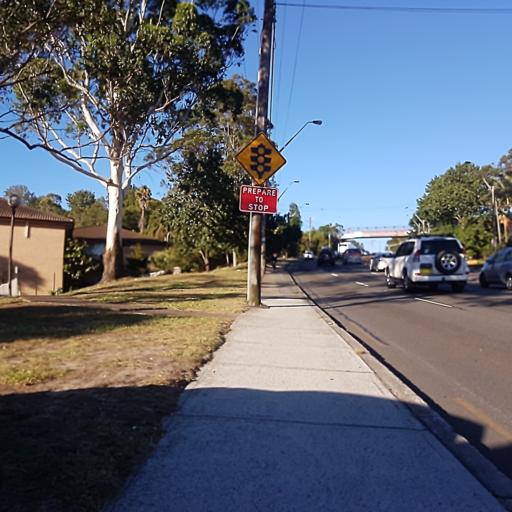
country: AU
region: New South Wales
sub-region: Warringah
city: Forestville
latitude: -33.7617
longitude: 151.2074
